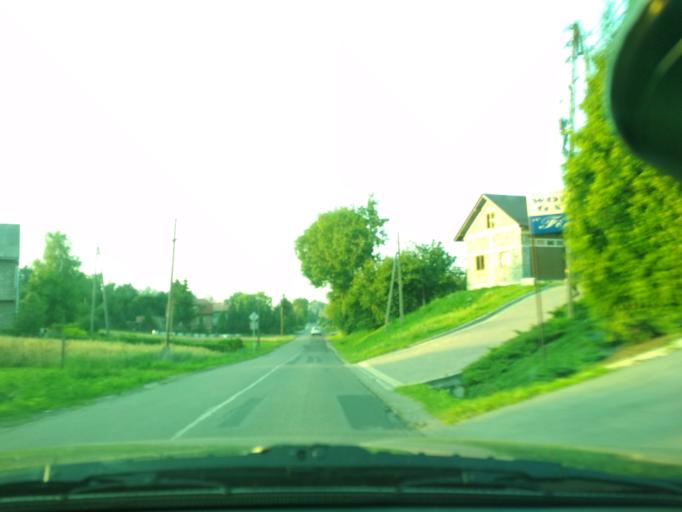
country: PL
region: Lesser Poland Voivodeship
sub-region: Powiat olkuski
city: Wolbrom
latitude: 50.4015
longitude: 19.7662
